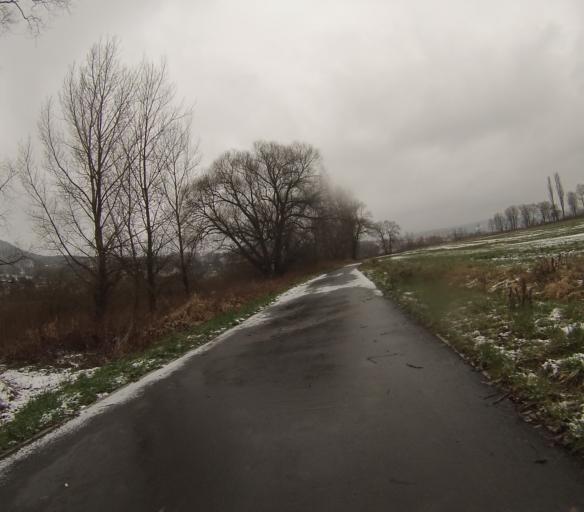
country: CZ
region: Ustecky
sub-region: Okres Decin
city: Decin
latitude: 50.7445
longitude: 14.1839
